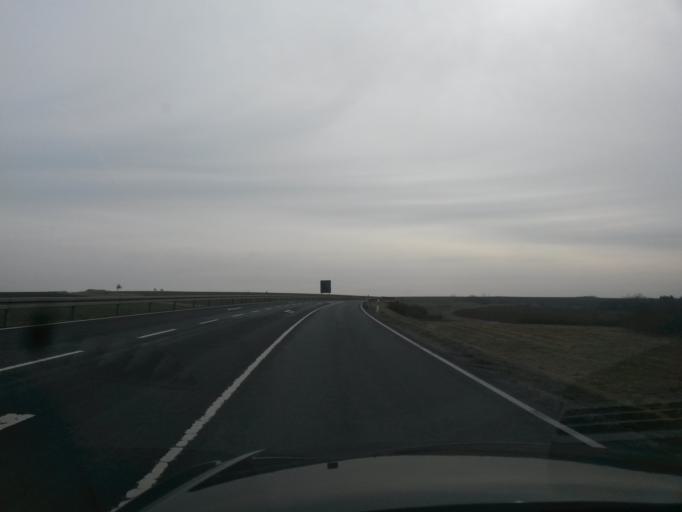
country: DE
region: Bavaria
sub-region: Regierungsbezirk Unterfranken
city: Mellrichstadt
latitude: 50.4268
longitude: 10.3348
